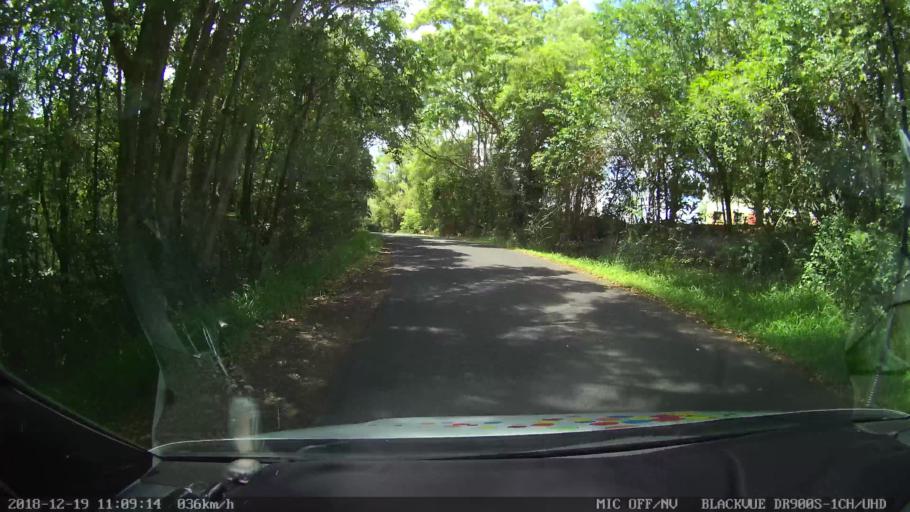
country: AU
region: New South Wales
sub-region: Lismore Municipality
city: Nimbin
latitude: -28.6335
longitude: 153.2639
